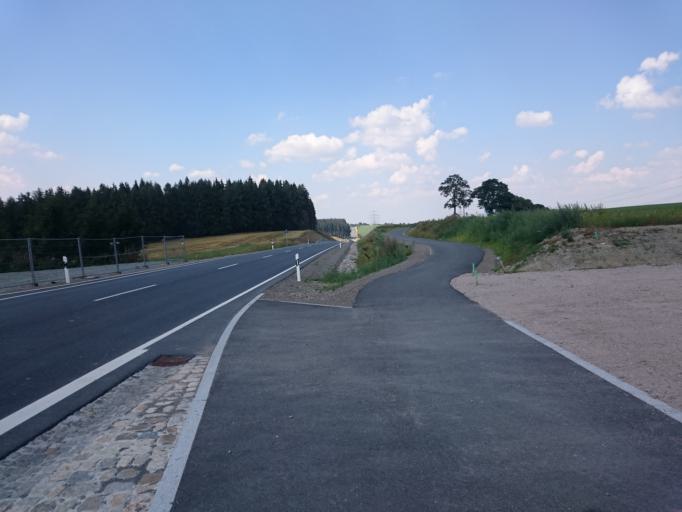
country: DE
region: Saxony
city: Dorfchemnitz
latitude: 50.6748
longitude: 12.8063
